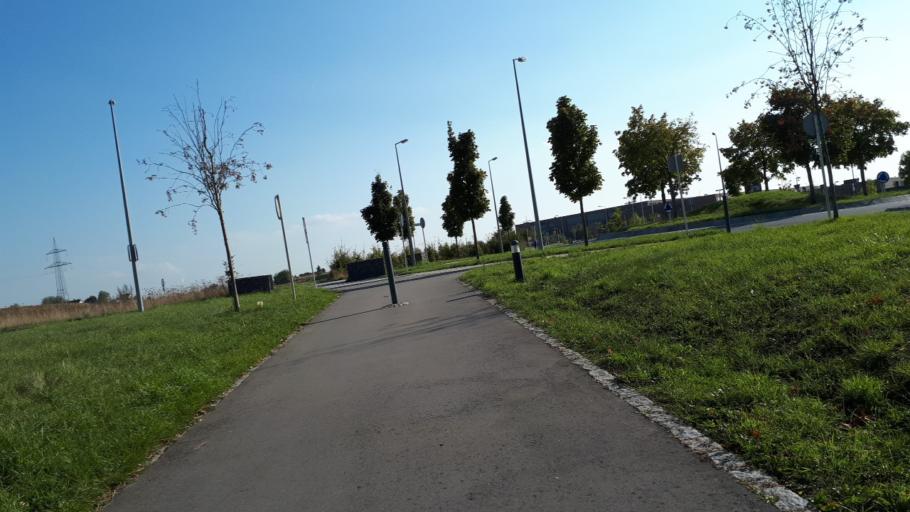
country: LU
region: Luxembourg
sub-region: Canton de Capellen
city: Mamer
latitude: 49.6210
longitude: 6.0371
